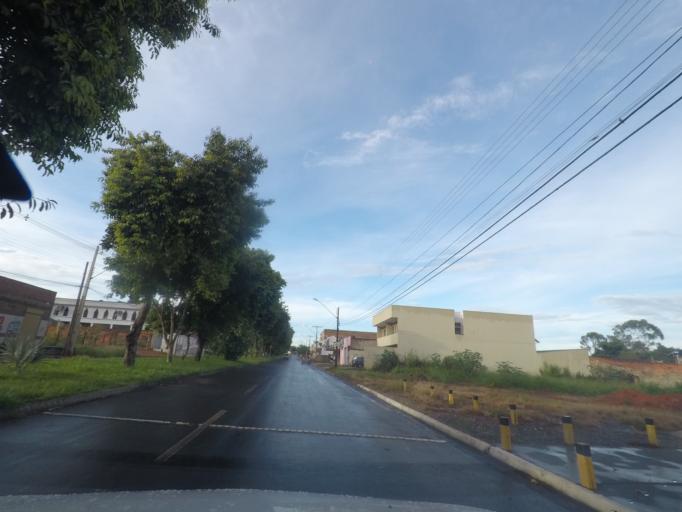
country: BR
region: Goias
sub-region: Goiania
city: Goiania
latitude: -16.7356
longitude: -49.3678
